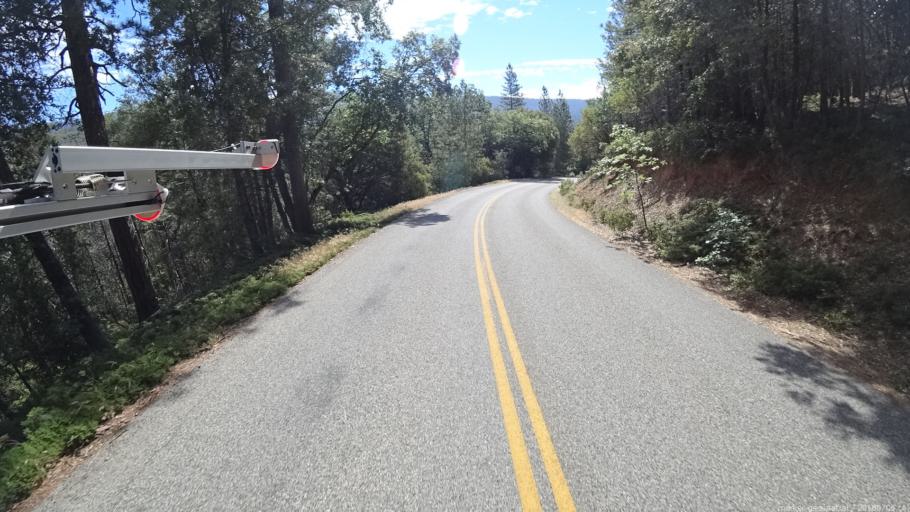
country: US
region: California
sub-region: Madera County
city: Oakhurst
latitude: 37.3284
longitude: -119.5570
